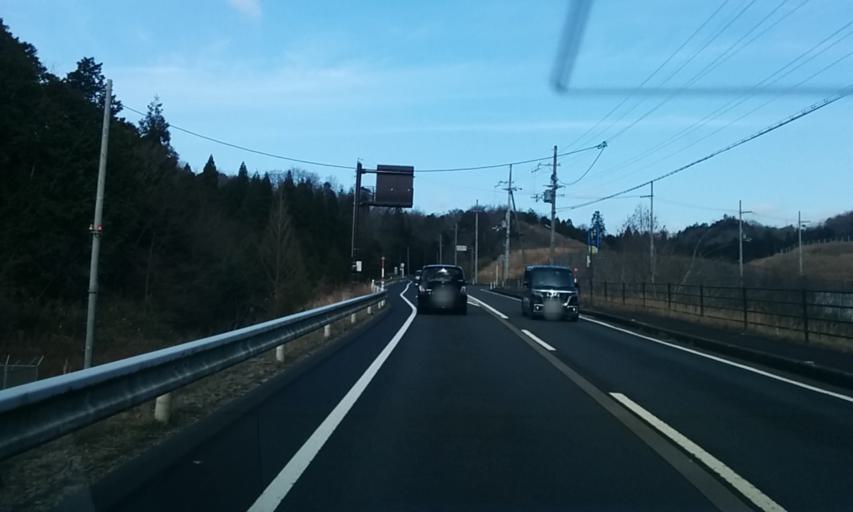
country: JP
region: Kyoto
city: Miyazu
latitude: 35.5789
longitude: 135.1202
